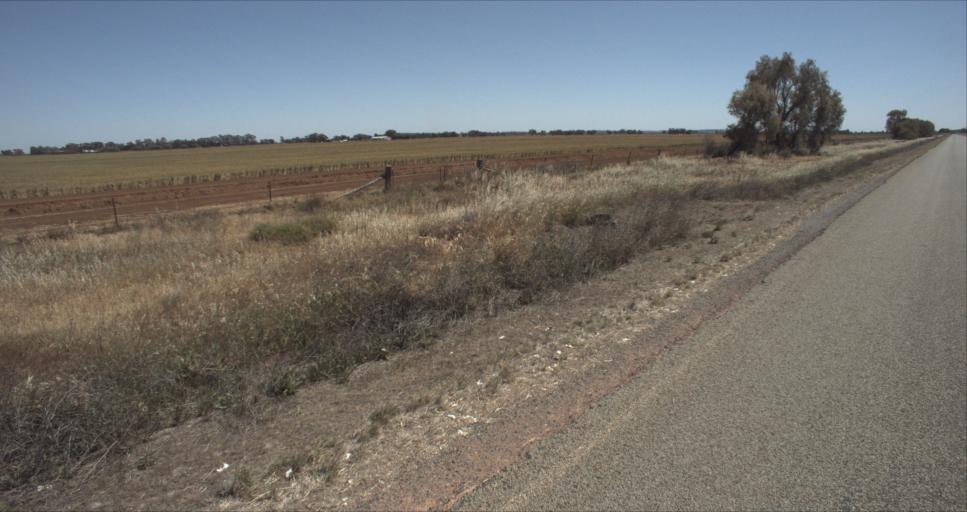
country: AU
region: New South Wales
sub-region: Leeton
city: Leeton
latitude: -34.4632
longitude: 146.2938
